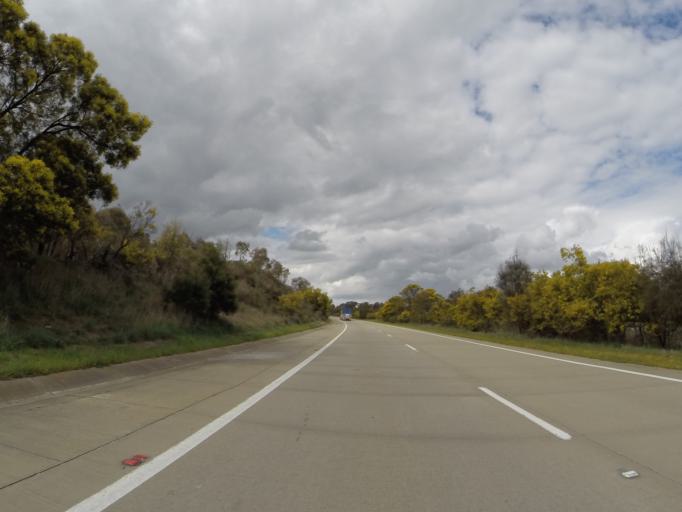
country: AU
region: New South Wales
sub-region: Goulburn Mulwaree
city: Goulburn
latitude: -34.8114
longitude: 149.4797
